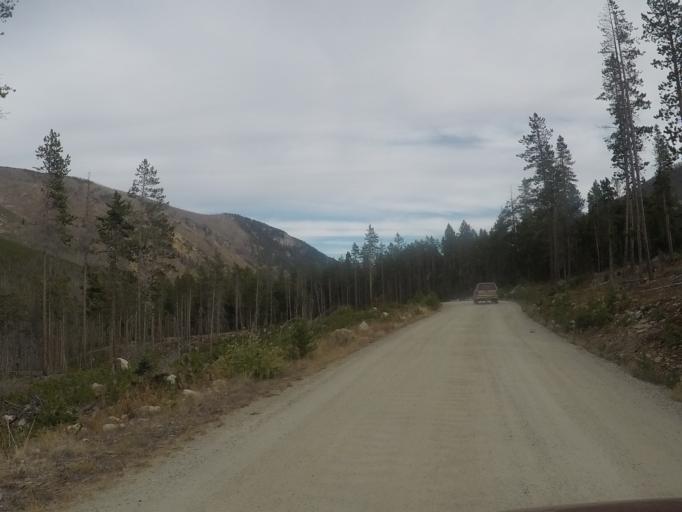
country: US
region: Montana
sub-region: Carbon County
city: Red Lodge
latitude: 45.1693
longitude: -109.4167
